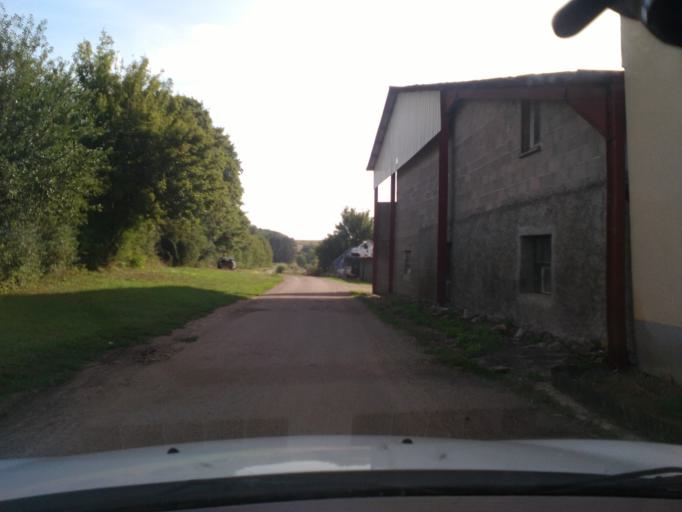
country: FR
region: Lorraine
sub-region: Departement des Vosges
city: Mirecourt
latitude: 48.3099
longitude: 6.0845
